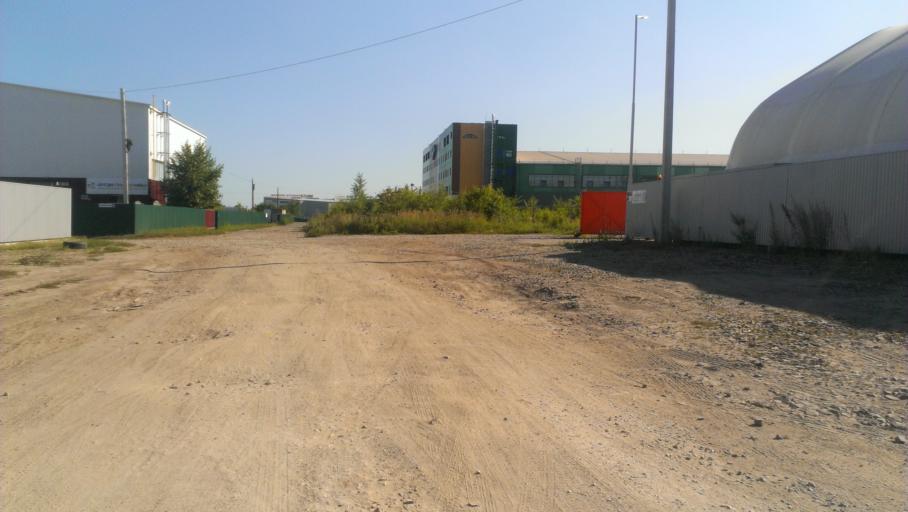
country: RU
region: Altai Krai
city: Novosilikatnyy
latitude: 53.3346
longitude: 83.6647
